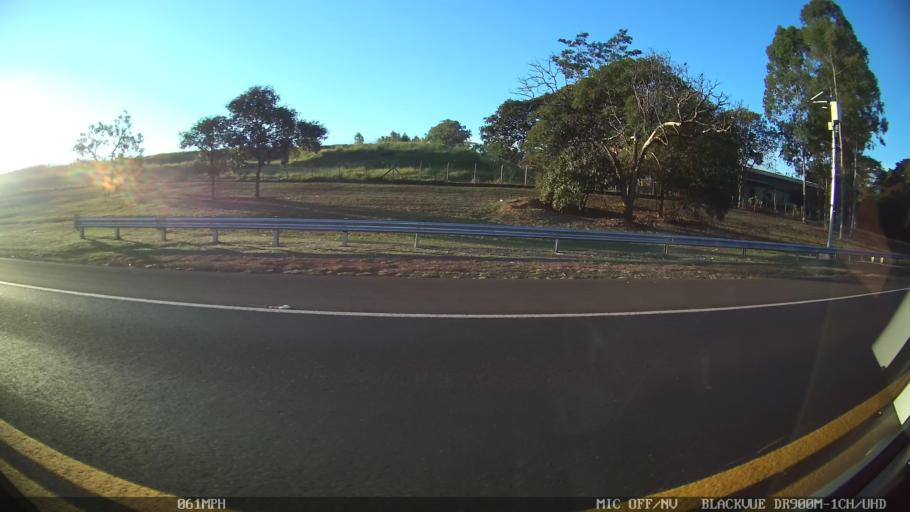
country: BR
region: Sao Paulo
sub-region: Araraquara
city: Araraquara
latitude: -21.8167
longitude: -48.2022
